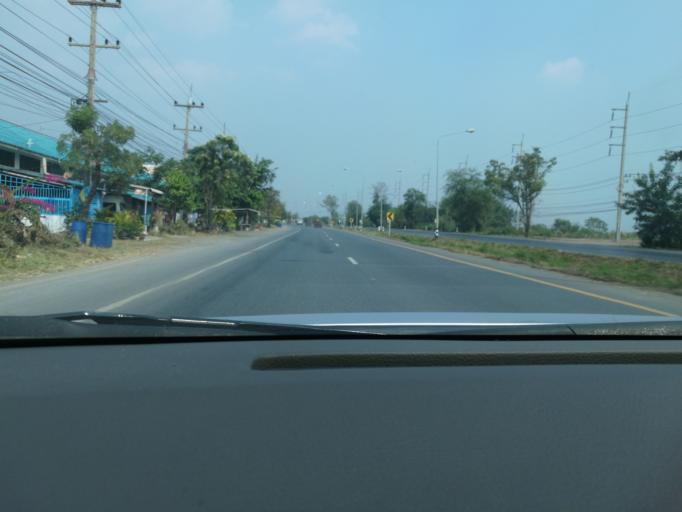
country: TH
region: Lop Buri
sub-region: Amphoe Tha Luang
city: Tha Luang
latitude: 15.0878
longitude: 101.0099
